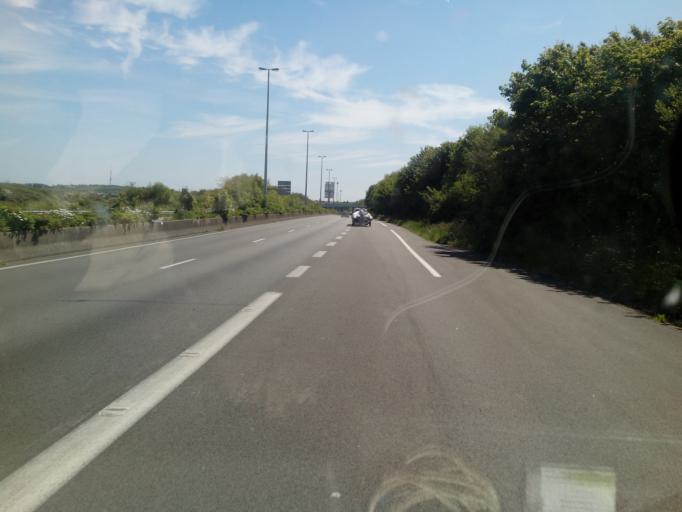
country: FR
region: Nord-Pas-de-Calais
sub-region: Departement du Pas-de-Calais
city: Wimille
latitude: 50.7456
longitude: 1.6278
